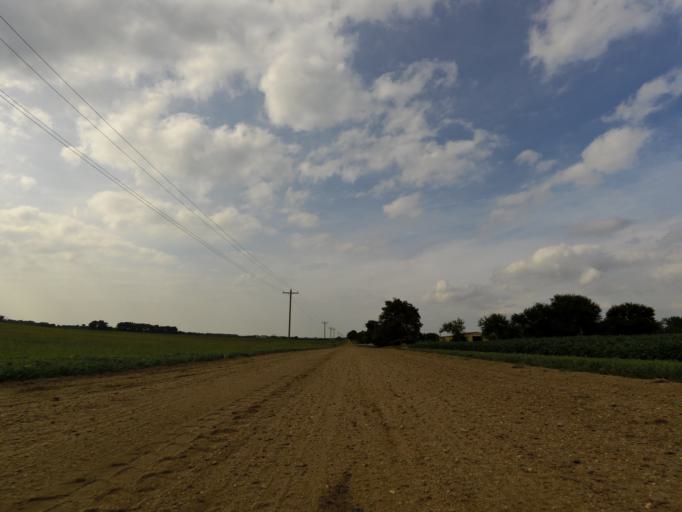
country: US
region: Kansas
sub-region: Reno County
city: South Hutchinson
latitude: 37.9024
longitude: -98.0688
